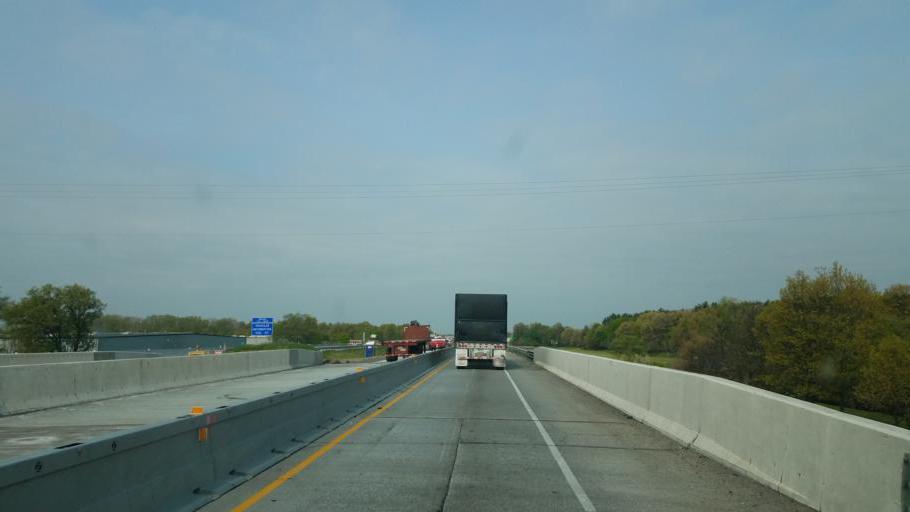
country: US
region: Indiana
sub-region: Elkhart County
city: Simonton Lake
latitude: 41.7307
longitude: -85.9462
